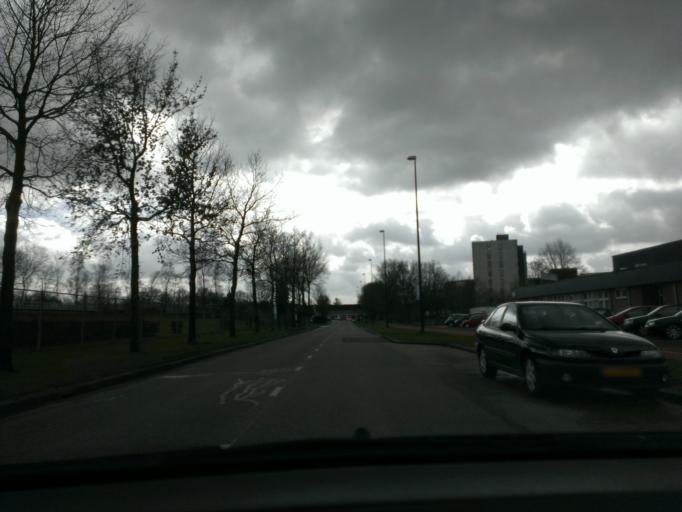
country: NL
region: Gelderland
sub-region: Gemeente Apeldoorn
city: Apeldoorn
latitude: 52.2379
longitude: 5.9698
